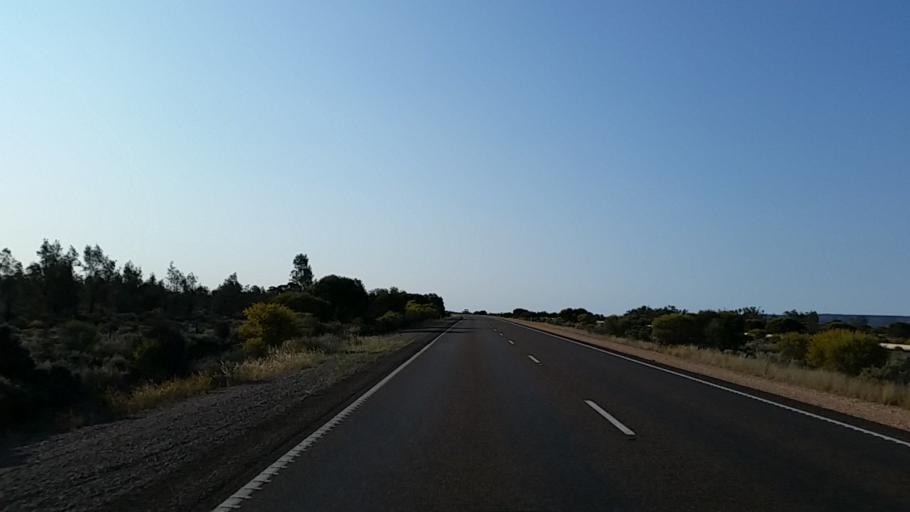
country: AU
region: South Australia
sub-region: Whyalla
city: Whyalla
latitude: -32.7902
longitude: 137.5368
